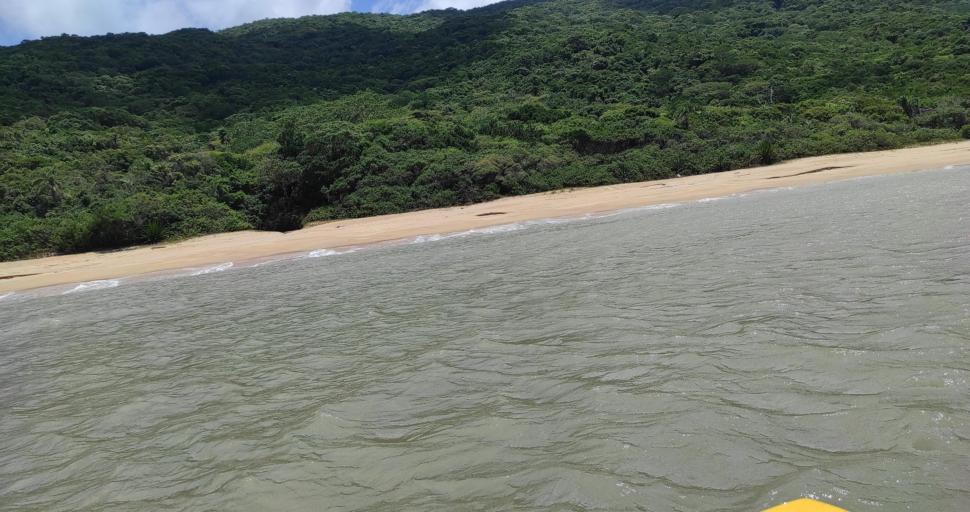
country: BR
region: Santa Catarina
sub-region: Porto Belo
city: Porto Belo
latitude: -27.2053
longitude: -48.5723
